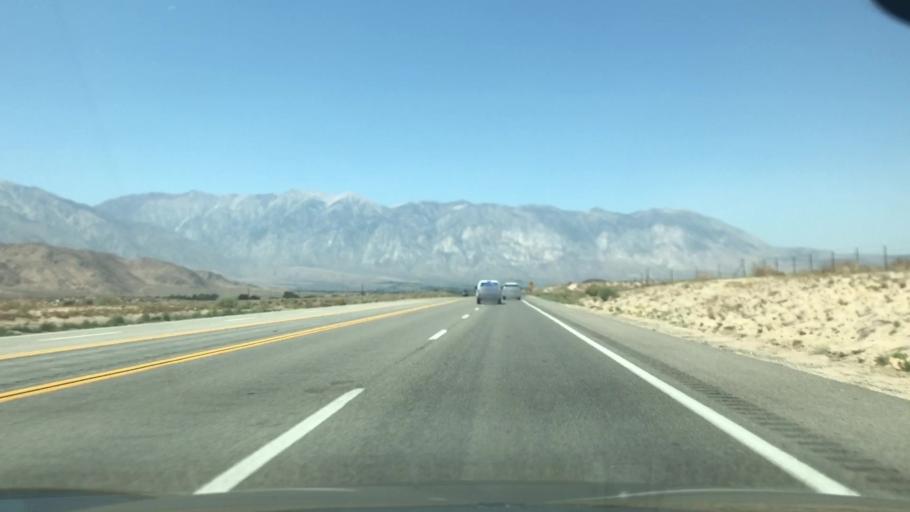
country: US
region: California
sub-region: Inyo County
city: West Bishop
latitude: 37.3790
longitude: -118.4717
